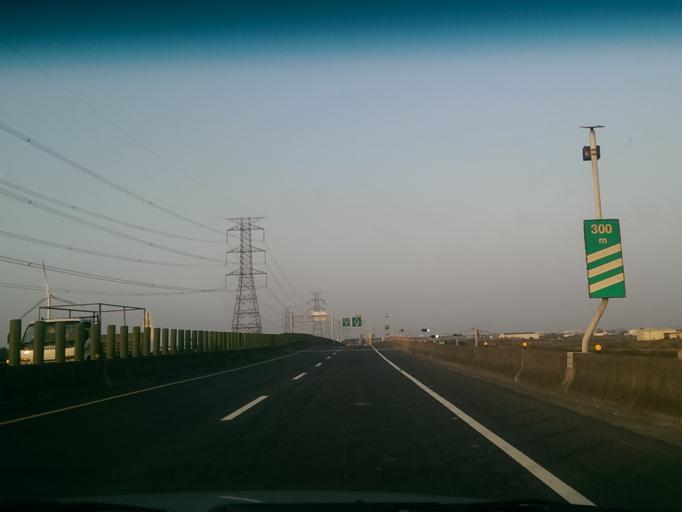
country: TW
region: Taiwan
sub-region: Changhua
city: Chang-hua
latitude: 24.1511
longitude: 120.4543
